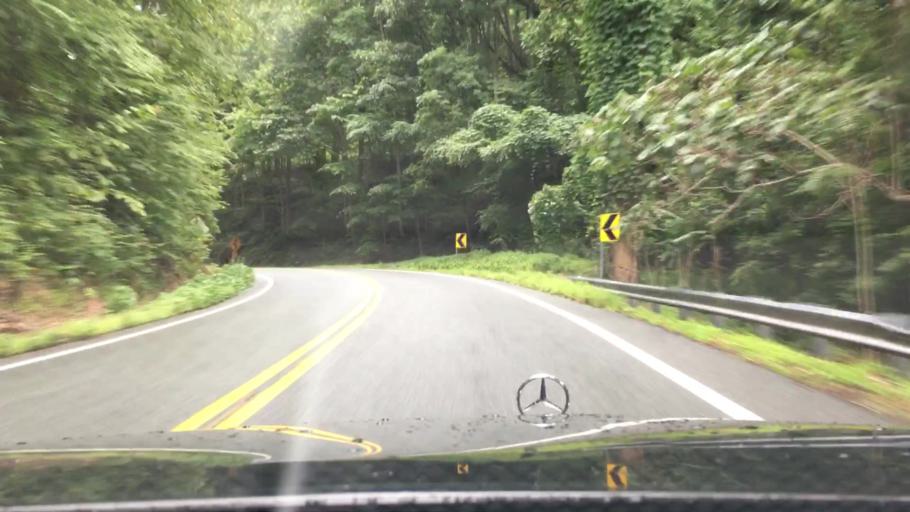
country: US
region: Virginia
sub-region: Nelson County
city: Nellysford
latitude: 37.8527
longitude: -78.9220
